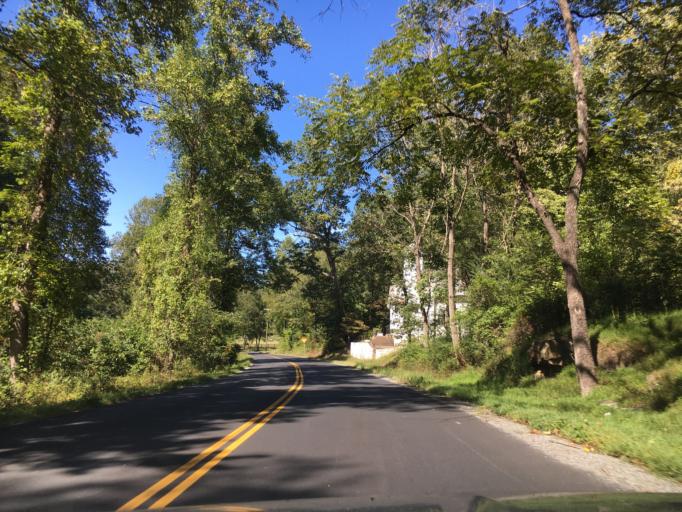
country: US
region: Virginia
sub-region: Albemarle County
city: Crozet
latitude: 37.9917
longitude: -78.7185
